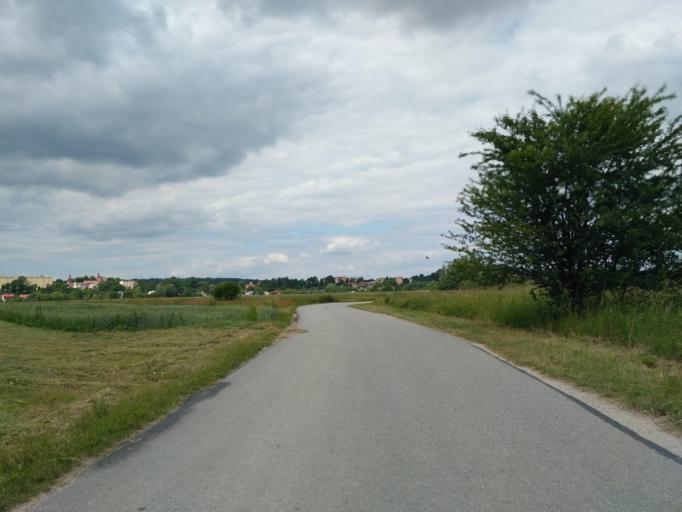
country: PL
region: Subcarpathian Voivodeship
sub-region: Powiat rzeszowski
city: Dynow
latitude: 49.8132
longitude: 22.2460
